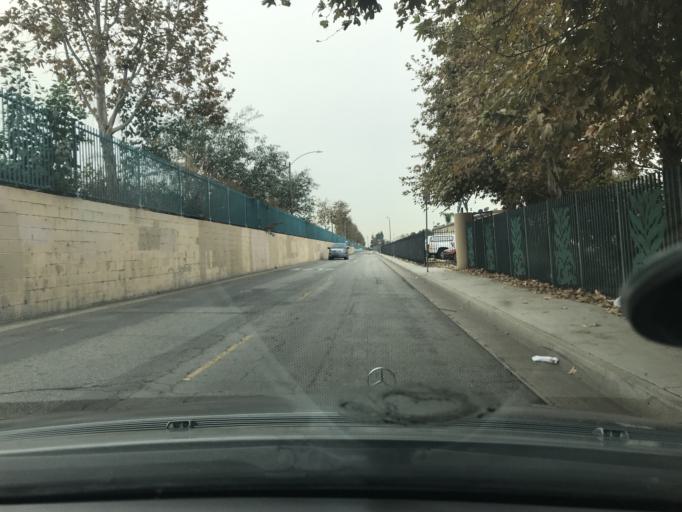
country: US
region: California
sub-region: Los Angeles County
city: Cudahy
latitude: 33.9633
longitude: -118.1720
